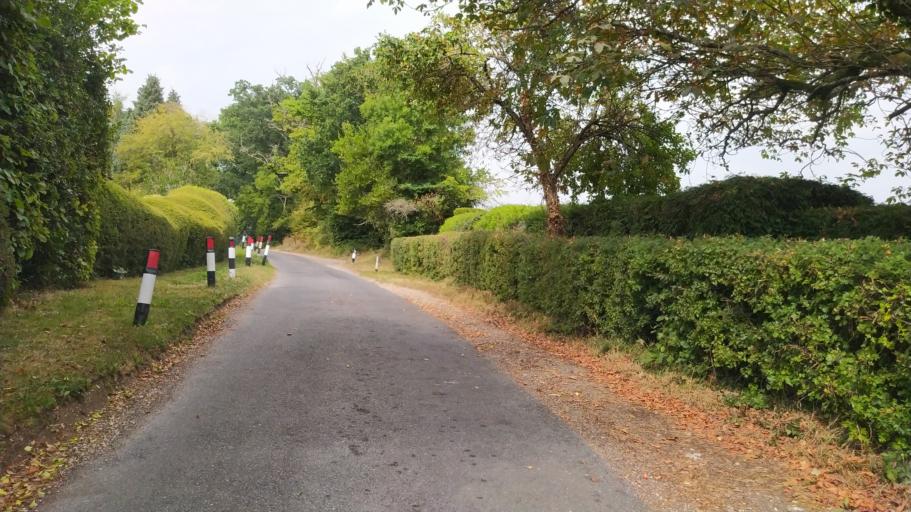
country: GB
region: England
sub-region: Hampshire
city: Chandlers Ford
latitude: 51.0032
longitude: -1.4353
